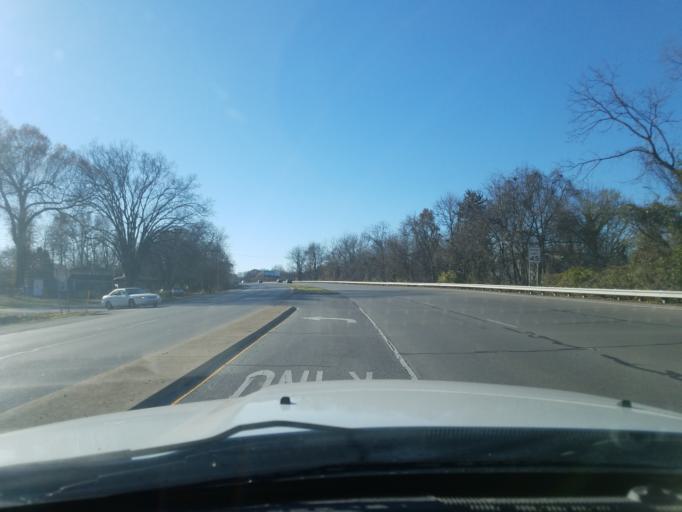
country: US
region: Indiana
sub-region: Clark County
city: Clarksville
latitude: 38.3031
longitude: -85.7843
